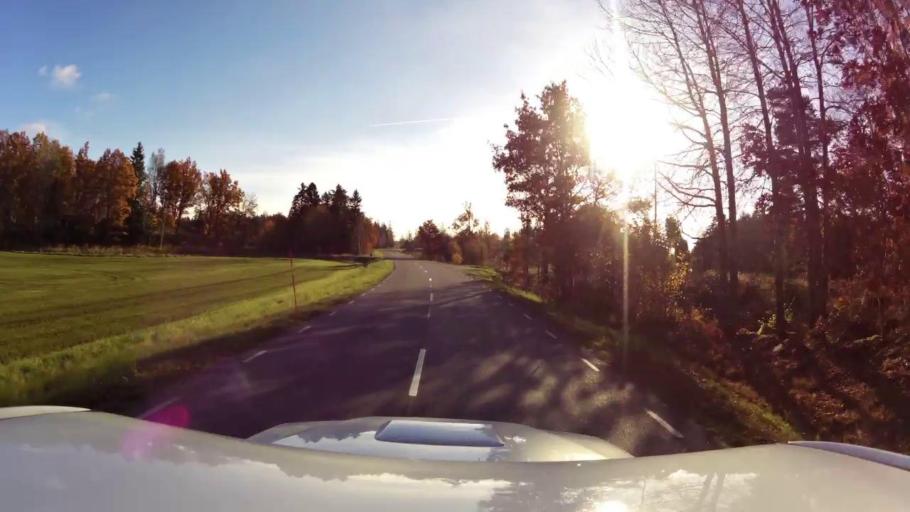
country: SE
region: OEstergoetland
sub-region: Linkopings Kommun
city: Vikingstad
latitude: 58.3123
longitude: 15.4903
